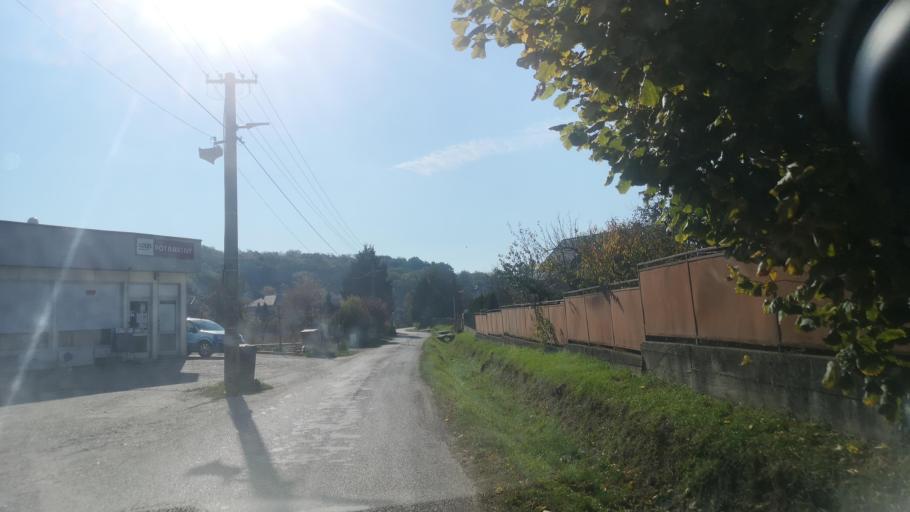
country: SK
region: Nitriansky
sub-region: Okres Nitra
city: Nitra
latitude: 48.2803
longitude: 17.9705
